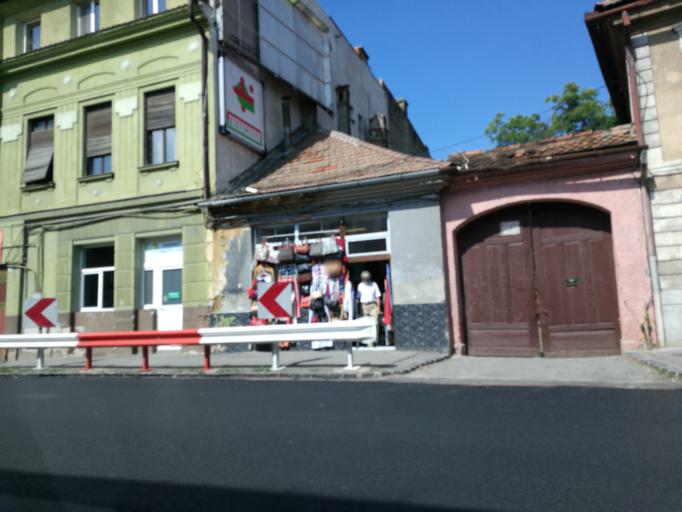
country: RO
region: Brasov
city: Brasov
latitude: 45.6484
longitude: 25.5986
